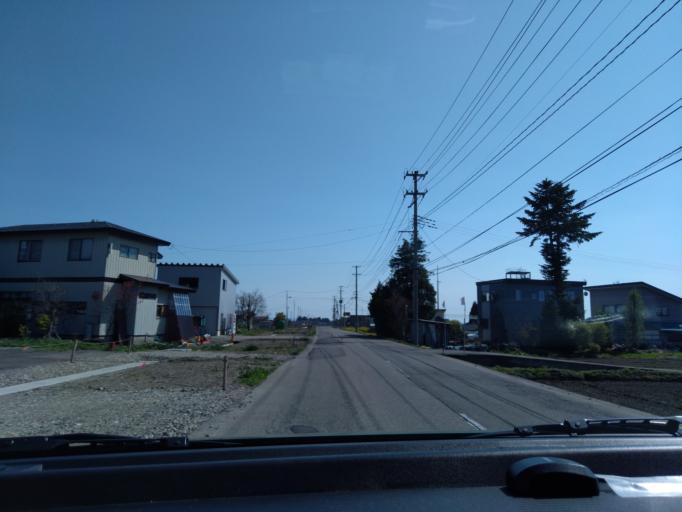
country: JP
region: Akita
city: Kakunodatemachi
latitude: 39.4852
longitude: 140.5911
